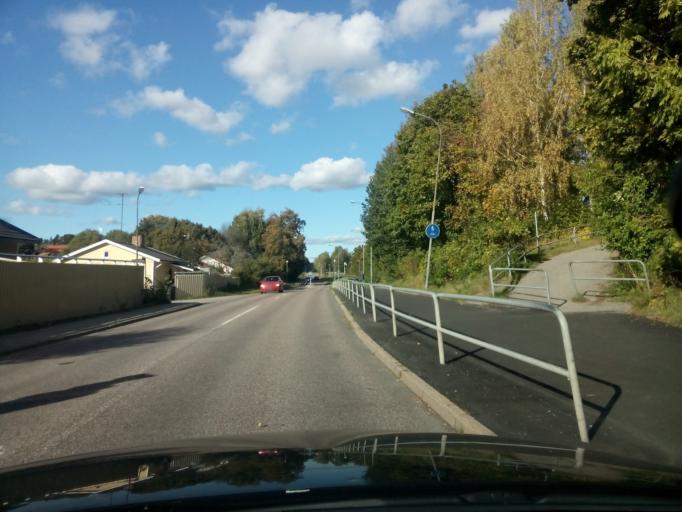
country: SE
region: Soedermanland
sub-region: Nykopings Kommun
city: Nykoping
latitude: 58.7624
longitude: 17.0087
